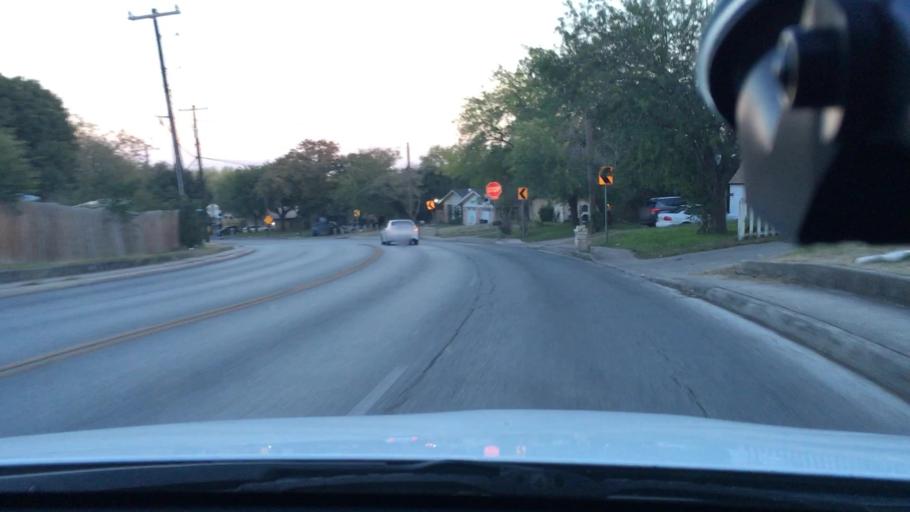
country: US
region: Texas
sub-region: Bexar County
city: Windcrest
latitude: 29.5114
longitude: -98.3602
